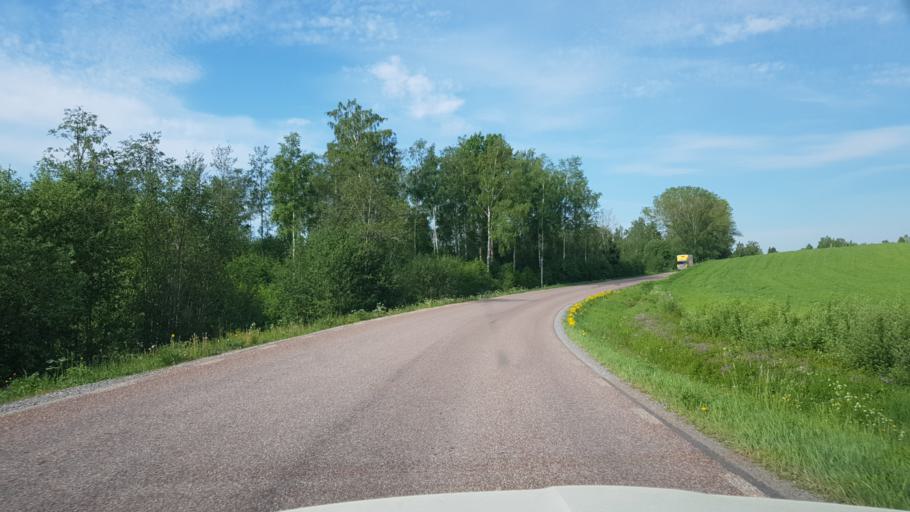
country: SE
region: Dalarna
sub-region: Borlange Kommun
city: Ornas
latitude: 60.4245
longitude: 15.6304
